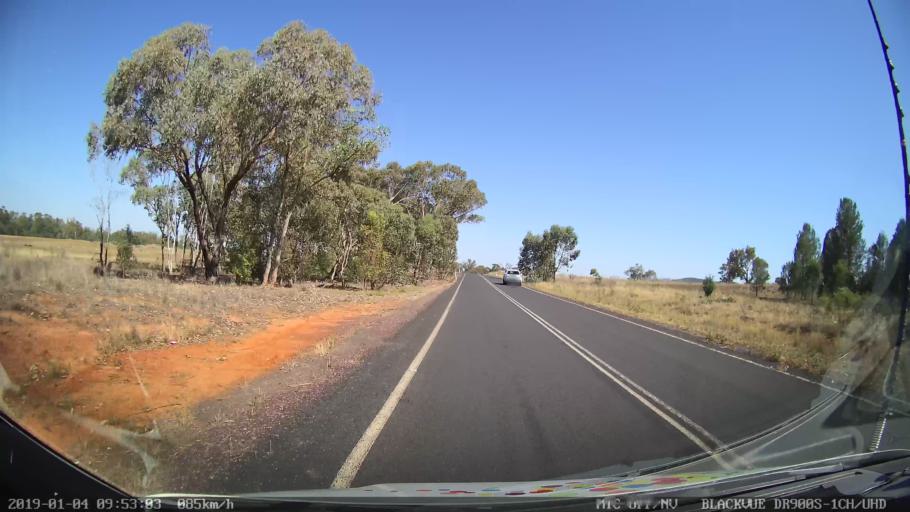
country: AU
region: New South Wales
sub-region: Cabonne
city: Canowindra
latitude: -33.5566
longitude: 148.4233
